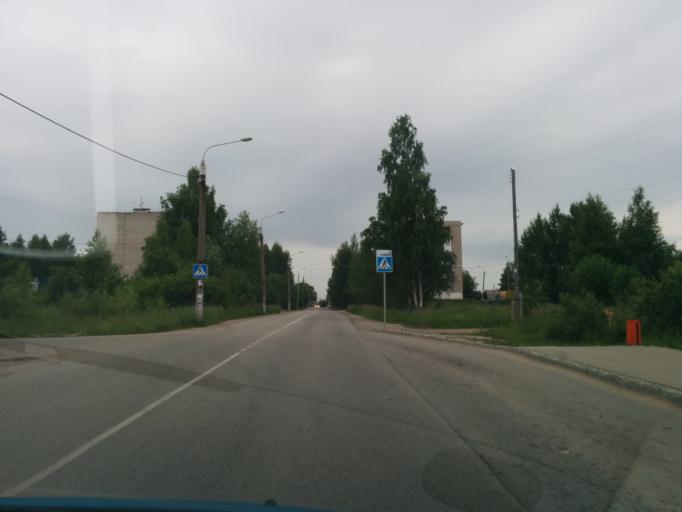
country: RU
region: Perm
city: Perm
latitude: 58.1580
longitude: 56.3051
